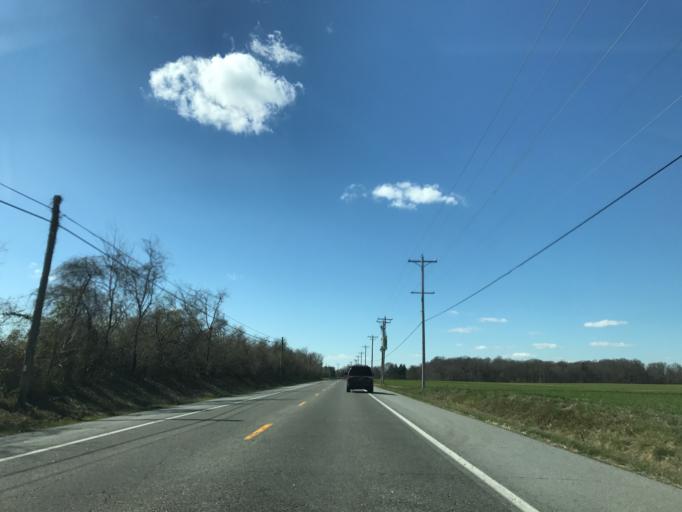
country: US
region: Maryland
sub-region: Kent County
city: Chestertown
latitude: 39.2211
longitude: -76.1540
